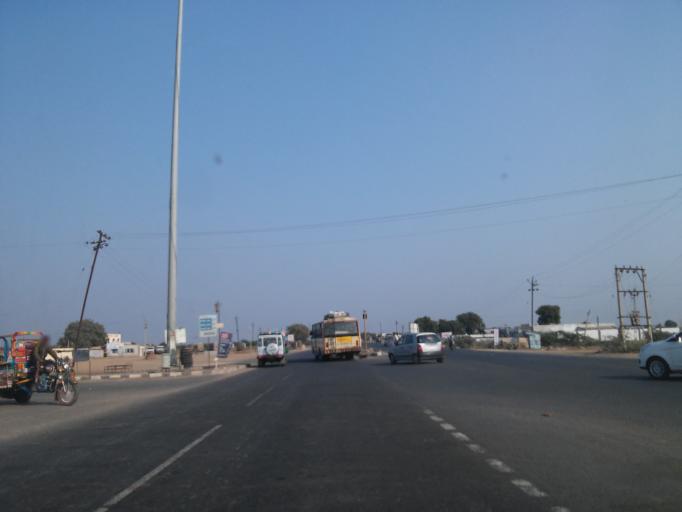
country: IN
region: Gujarat
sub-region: Surendranagar
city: Halvad
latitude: 23.0041
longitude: 71.1652
